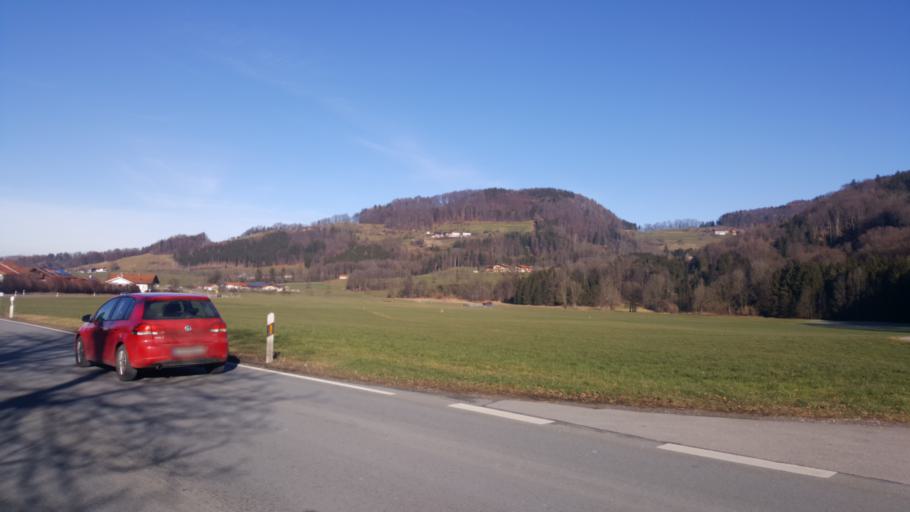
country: DE
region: Bavaria
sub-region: Upper Bavaria
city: Nussdorf am Inn
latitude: 47.7456
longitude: 12.1530
